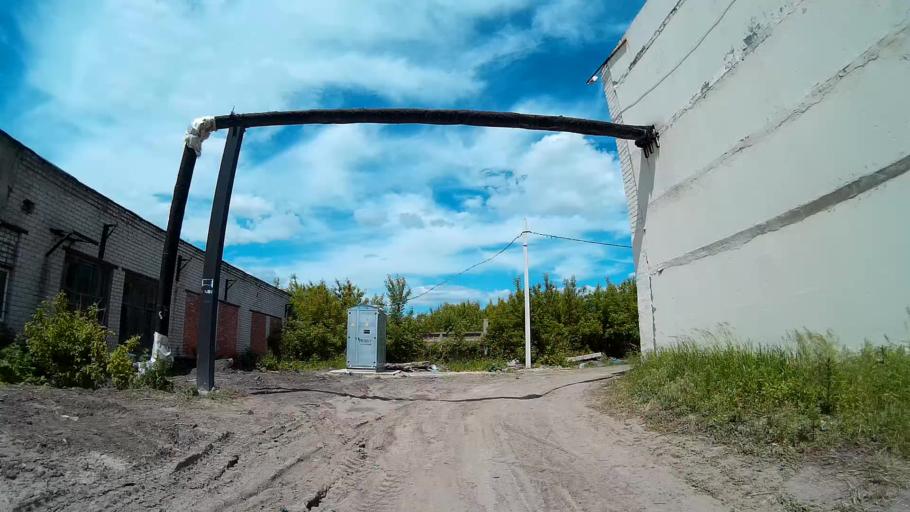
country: RU
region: Ulyanovsk
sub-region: Ulyanovskiy Rayon
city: Ulyanovsk
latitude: 54.2788
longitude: 48.3531
